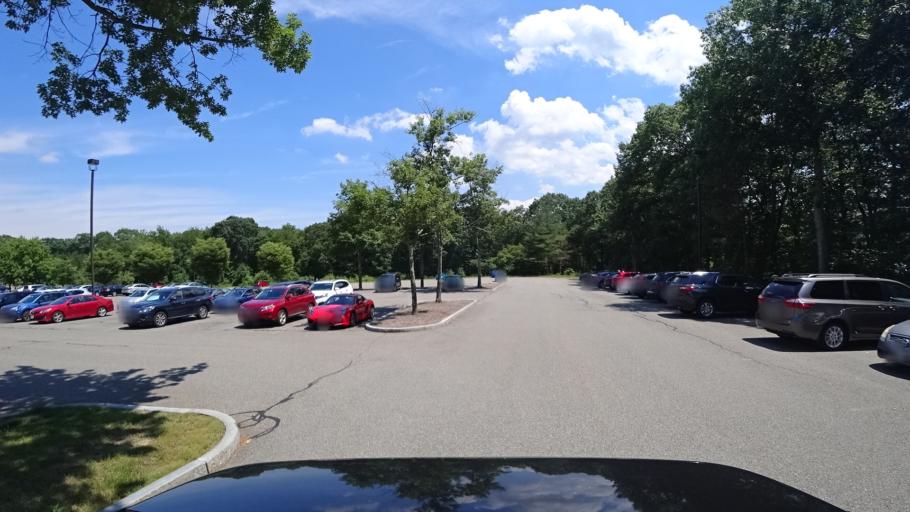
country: US
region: Massachusetts
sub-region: Norfolk County
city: Westwood
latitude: 42.2386
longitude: -71.2086
